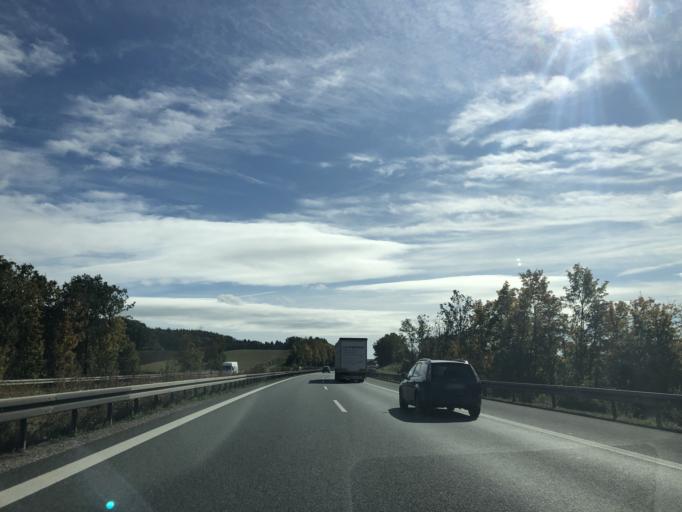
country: DE
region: Bavaria
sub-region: Upper Palatinate
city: Pilsach
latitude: 49.3379
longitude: 11.4523
